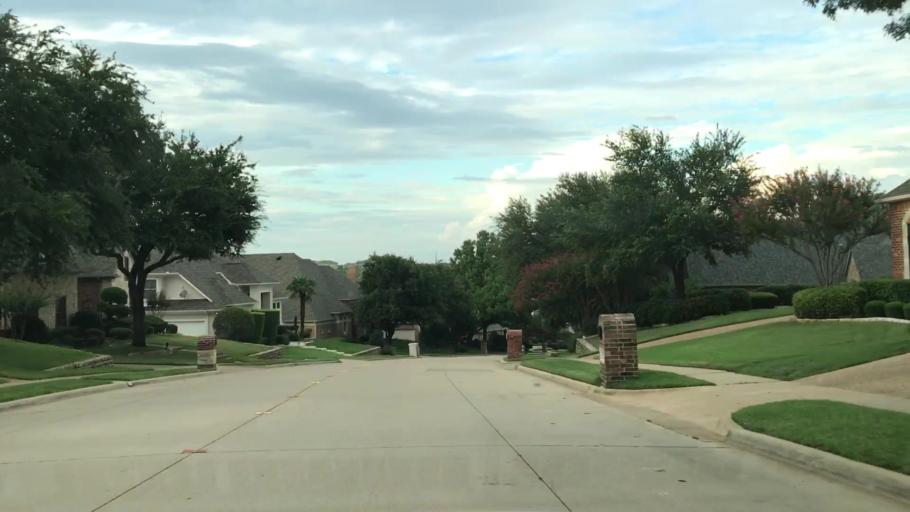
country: US
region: Texas
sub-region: Denton County
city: The Colony
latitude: 33.0418
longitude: -96.8501
